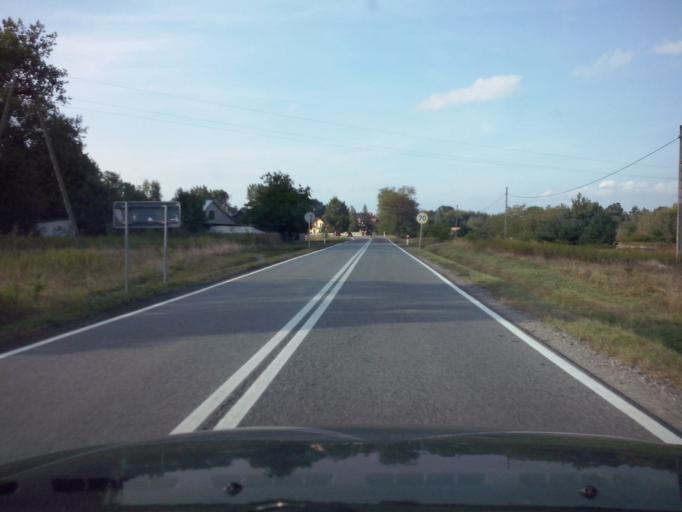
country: PL
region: Subcarpathian Voivodeship
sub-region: Powiat nizanski
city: Krzeszow
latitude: 50.3654
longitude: 22.3216
